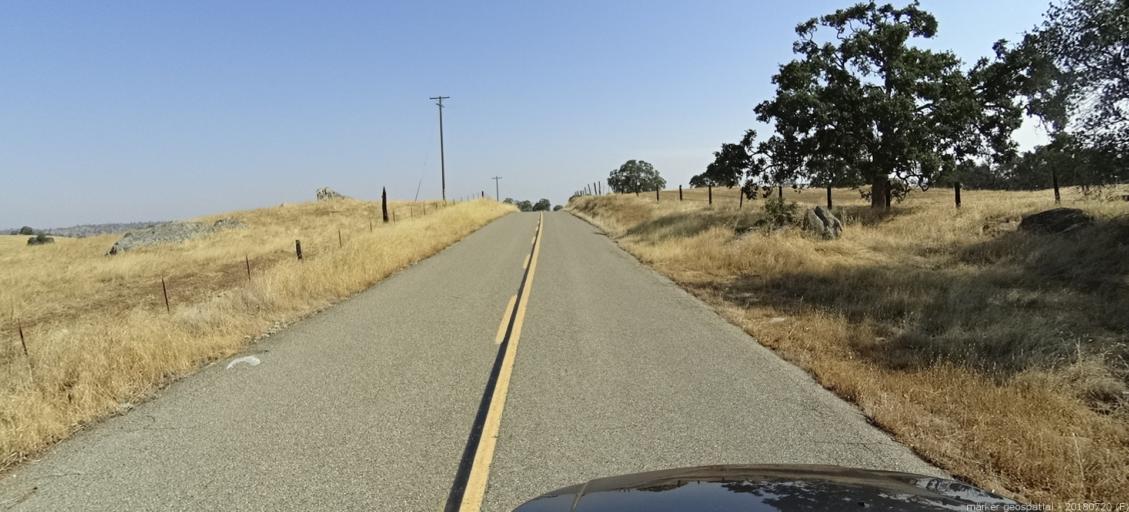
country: US
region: California
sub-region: Madera County
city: Yosemite Lakes
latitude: 37.2549
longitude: -119.9249
